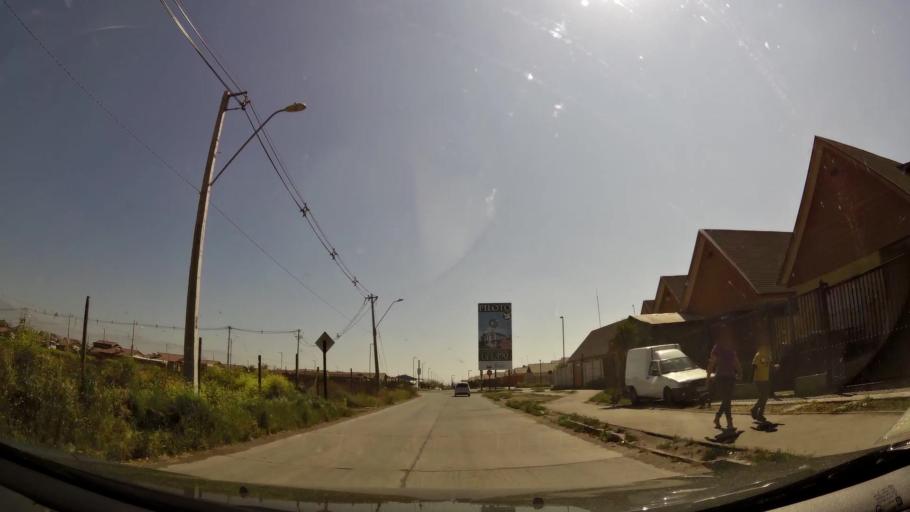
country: CL
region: Santiago Metropolitan
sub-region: Provincia de Chacabuco
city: Lampa
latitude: -33.3270
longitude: -70.7653
